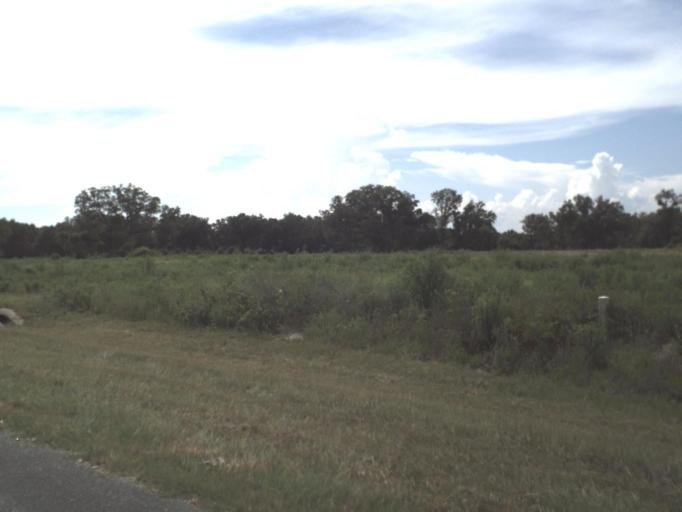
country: US
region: Florida
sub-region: Taylor County
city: Perry
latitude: 30.0811
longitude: -83.5150
